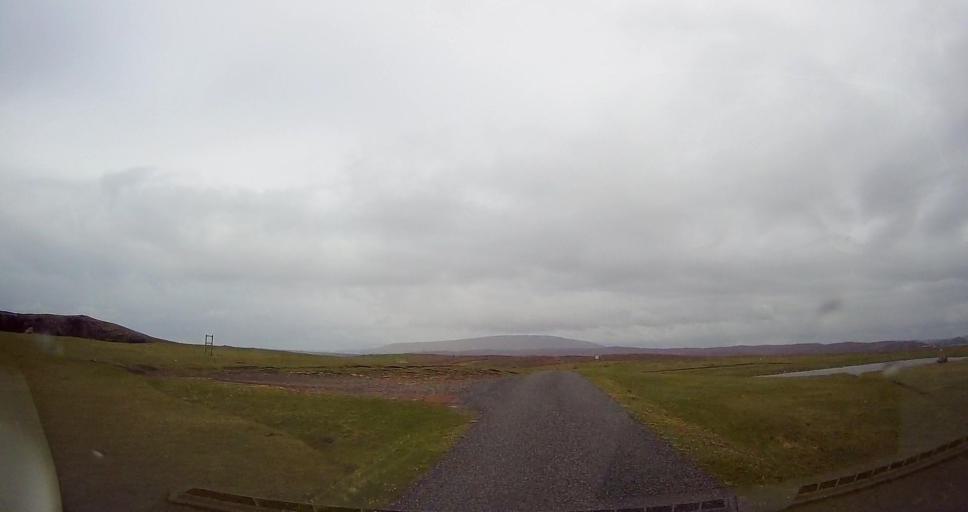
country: GB
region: Scotland
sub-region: Shetland Islands
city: Lerwick
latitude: 60.4889
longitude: -1.6251
